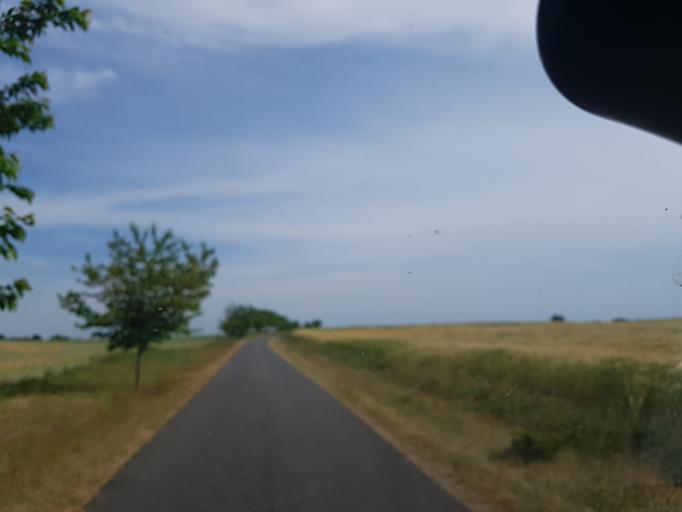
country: DE
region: Saxony-Anhalt
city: Kropstadt
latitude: 51.9962
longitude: 12.6738
